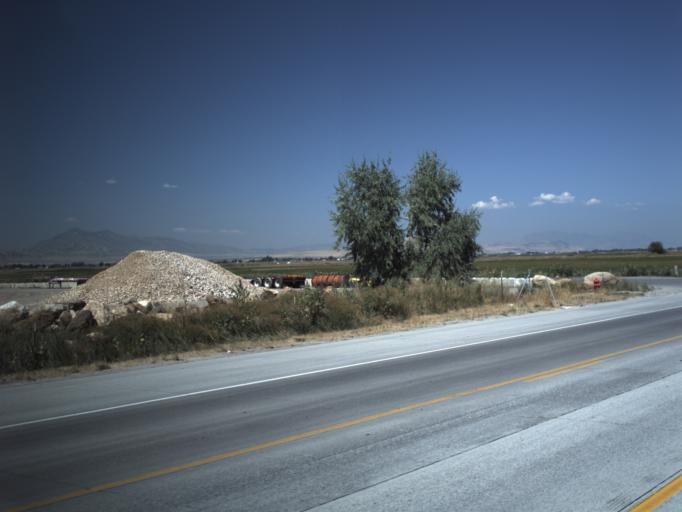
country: US
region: Utah
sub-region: Cache County
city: Logan
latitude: 41.7730
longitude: -111.8584
